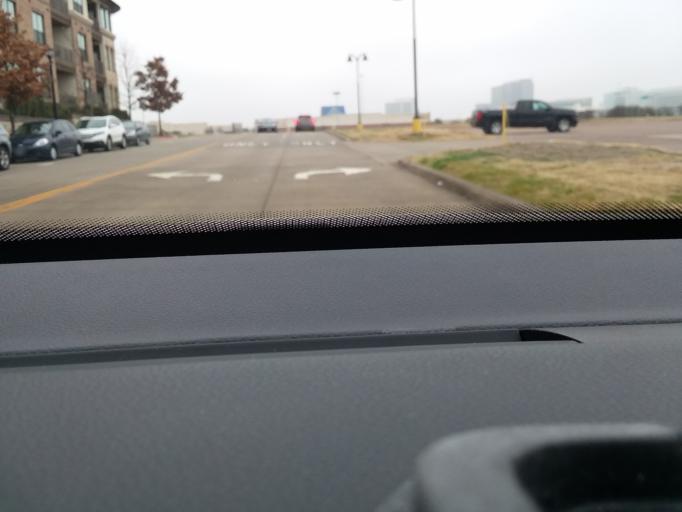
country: US
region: Texas
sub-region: Collin County
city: Frisco
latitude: 33.0972
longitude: -96.8188
